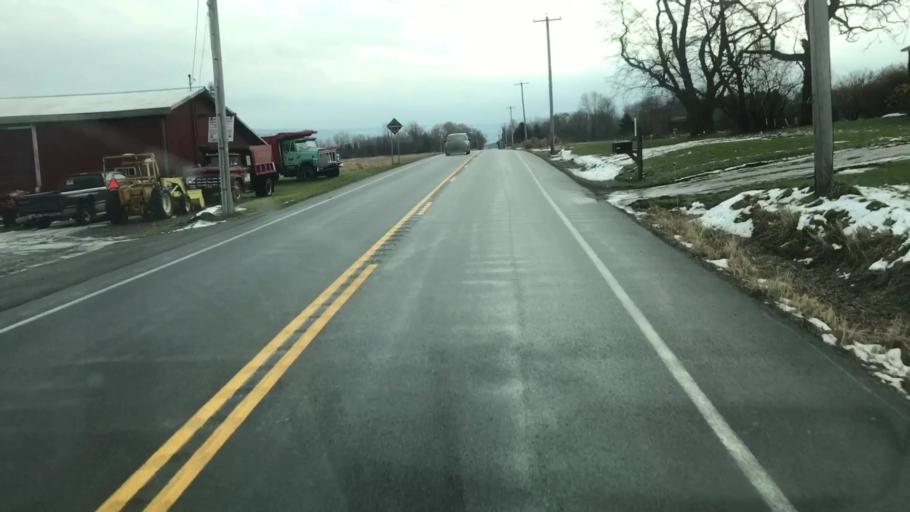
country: US
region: New York
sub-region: Onondaga County
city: Skaneateles
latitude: 42.8387
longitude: -76.3675
